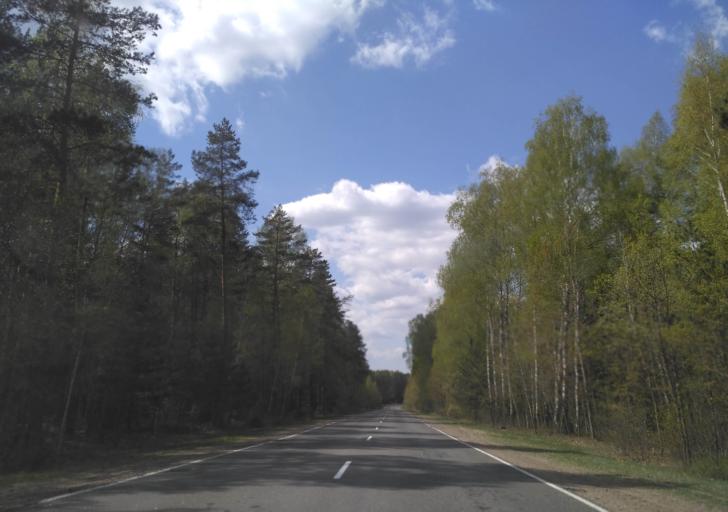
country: BY
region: Minsk
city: Vilyeyka
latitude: 54.4988
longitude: 27.1006
